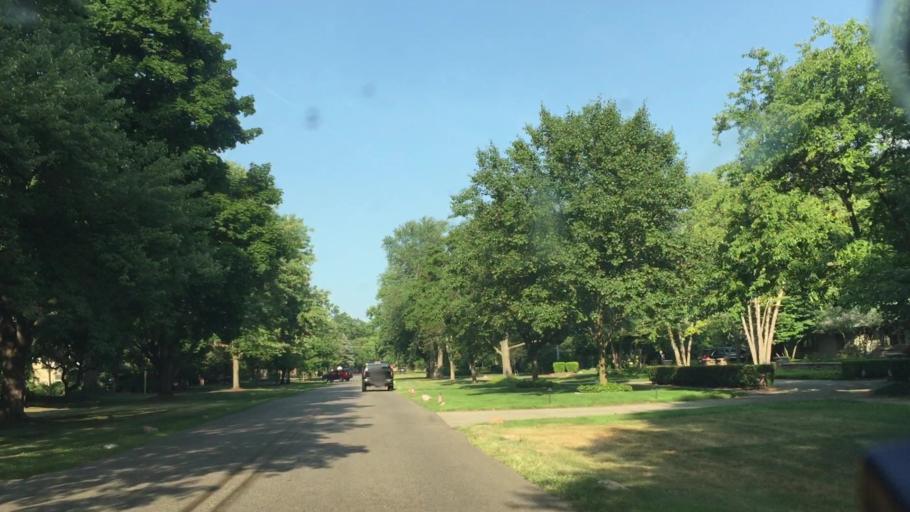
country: US
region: Michigan
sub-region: Oakland County
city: Beverly Hills
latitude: 42.5301
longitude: -83.2351
